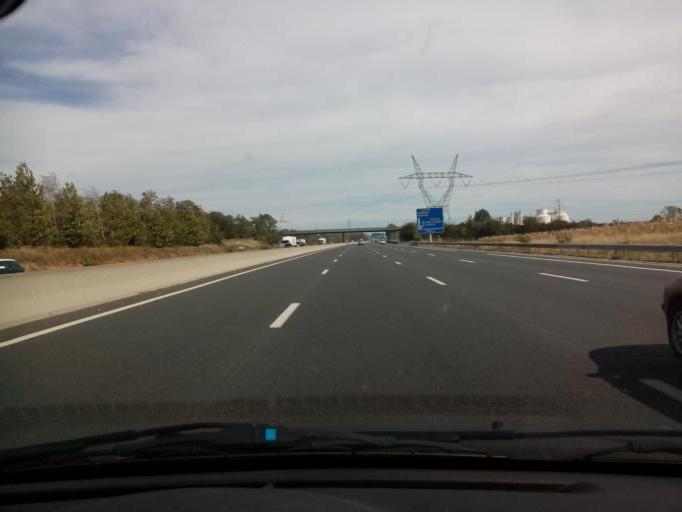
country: FR
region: Rhone-Alpes
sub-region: Departement du Rhone
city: Saint-Bonnet-de-Mure
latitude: 45.6791
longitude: 5.0245
